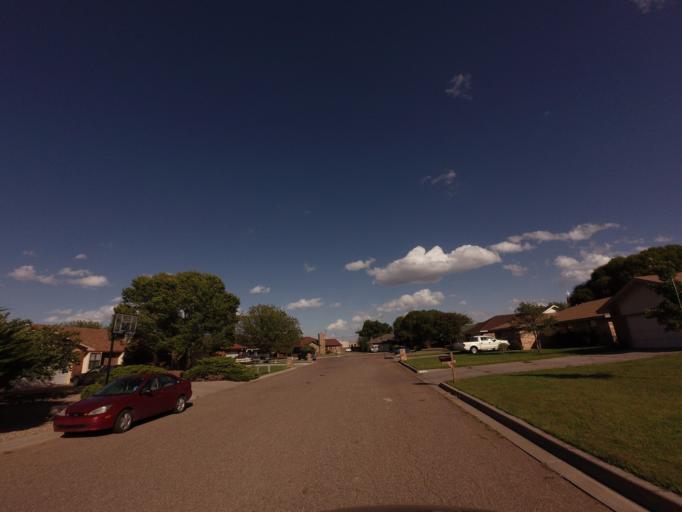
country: US
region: New Mexico
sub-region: Curry County
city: Clovis
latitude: 34.4344
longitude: -103.1800
